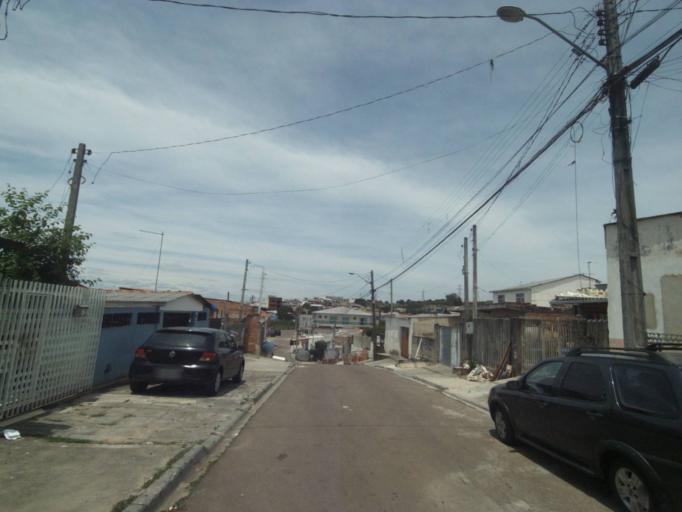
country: BR
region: Parana
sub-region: Curitiba
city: Curitiba
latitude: -25.5010
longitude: -49.3398
